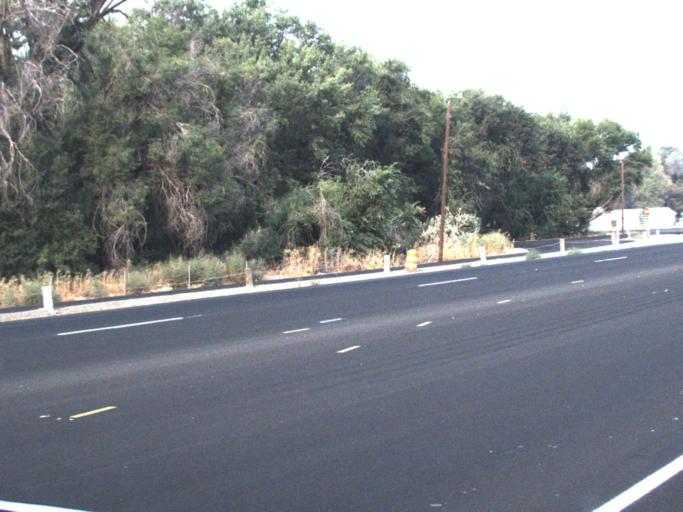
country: US
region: Washington
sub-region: Yakima County
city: Wapato
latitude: 46.4183
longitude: -120.3978
